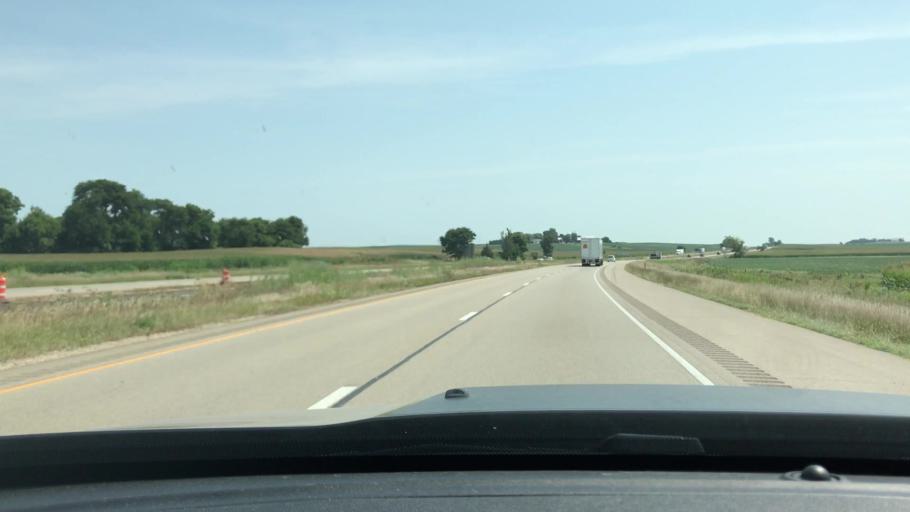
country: US
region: Illinois
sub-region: Bureau County
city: Walnut
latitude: 41.3892
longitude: -89.6705
